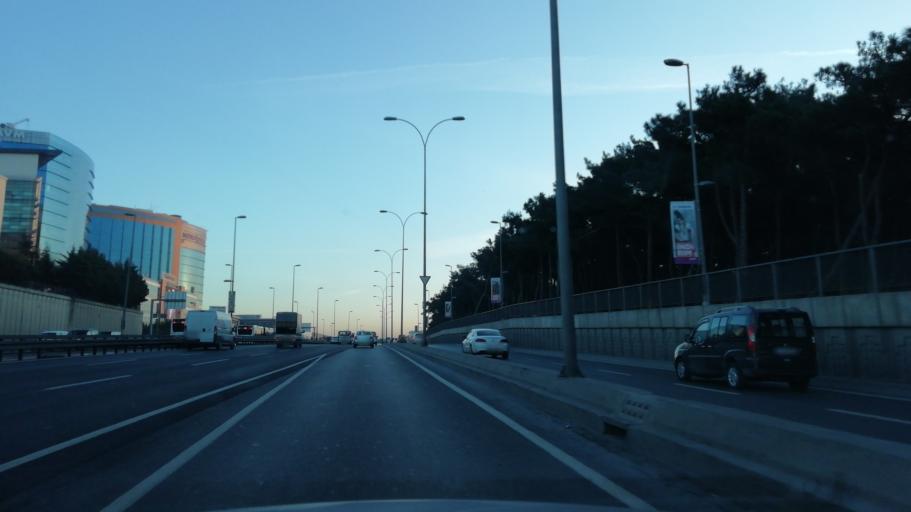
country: TR
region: Istanbul
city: Bahcelievler
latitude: 40.9939
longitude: 28.8603
